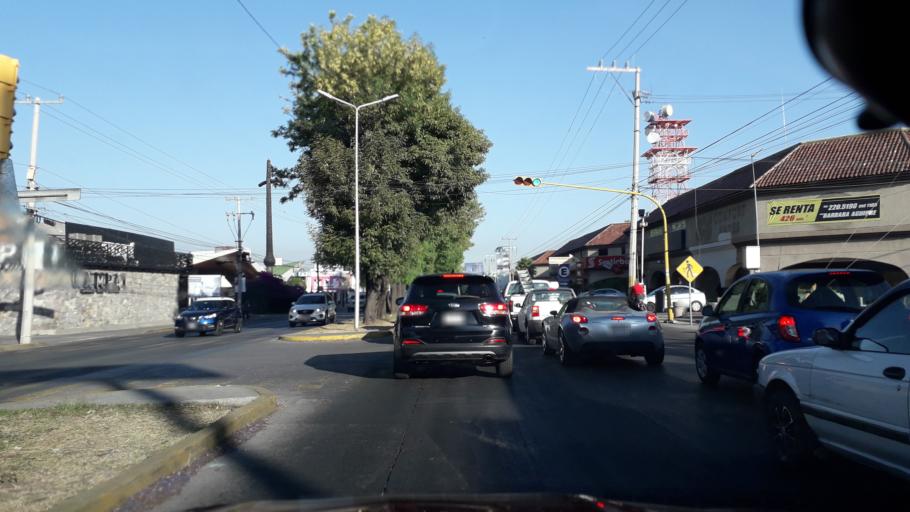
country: MX
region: Puebla
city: Puebla
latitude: 19.0421
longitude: -98.2311
